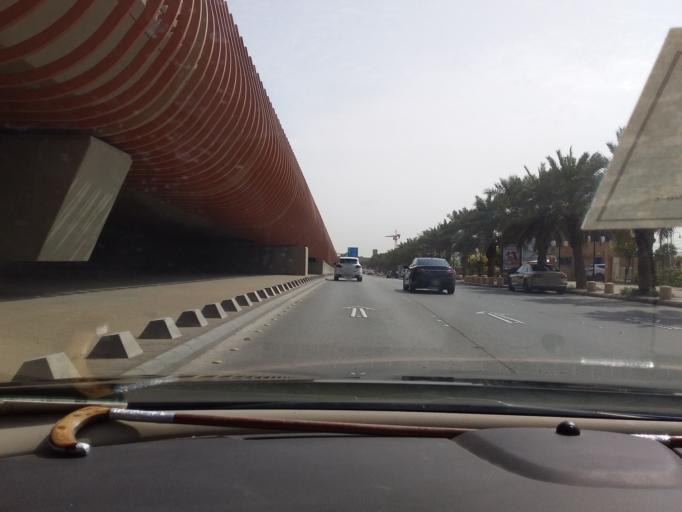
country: SA
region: Ar Riyad
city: Riyadh
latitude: 24.7427
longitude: 46.7037
